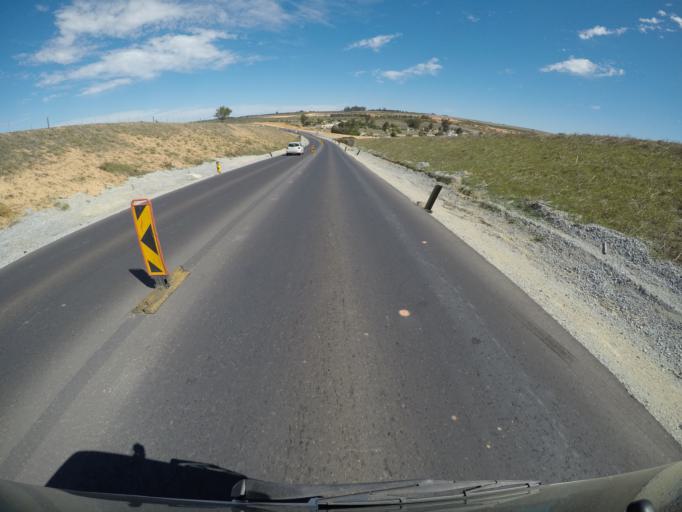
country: ZA
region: Western Cape
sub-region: West Coast District Municipality
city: Malmesbury
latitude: -33.4818
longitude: 18.6787
